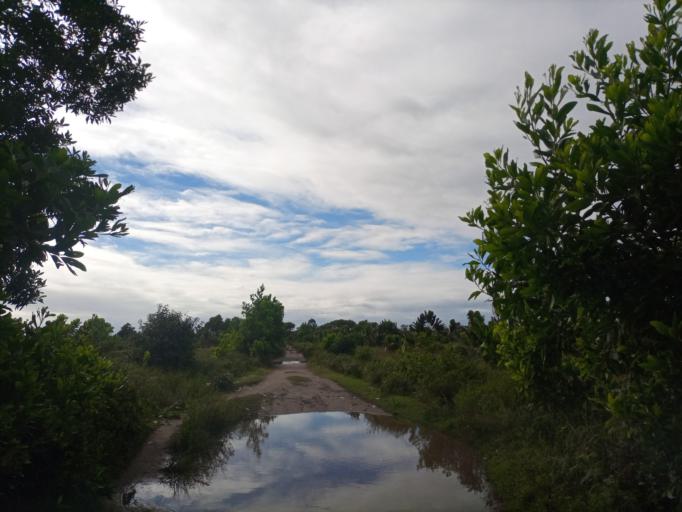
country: MG
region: Anosy
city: Fort Dauphin
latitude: -24.7794
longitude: 47.1851
